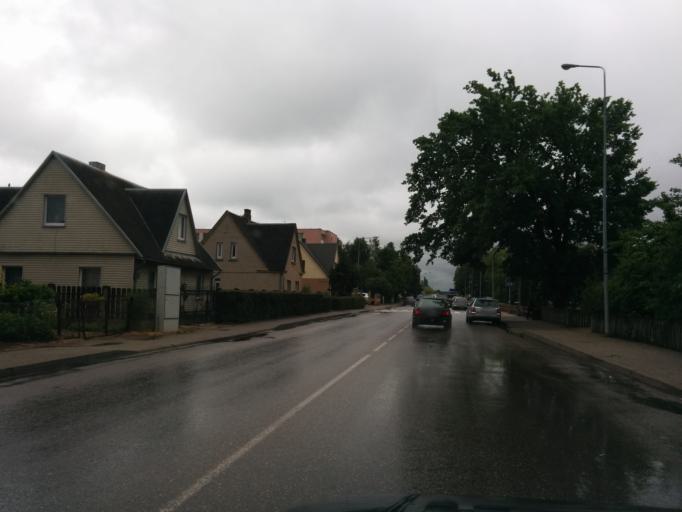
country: LT
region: Panevezys
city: Pasvalys
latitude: 56.0582
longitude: 24.4054
